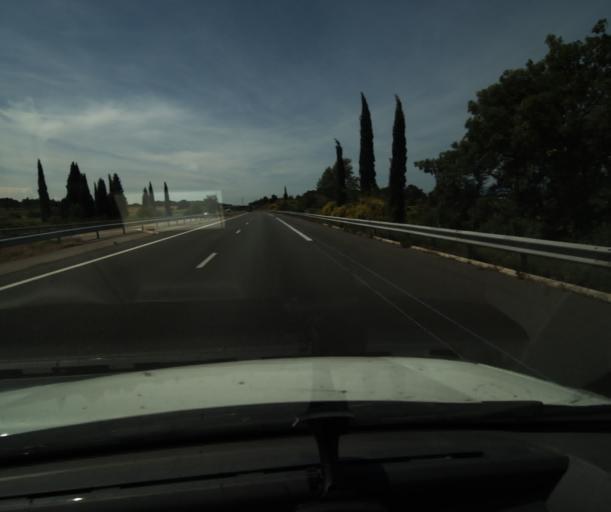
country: FR
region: Languedoc-Roussillon
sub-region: Departement de l'Aude
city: Trebes
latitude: 43.1929
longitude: 2.4530
